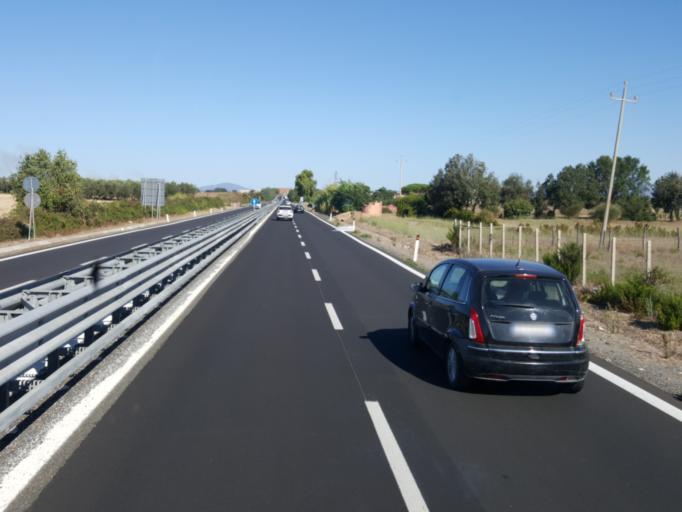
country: IT
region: Latium
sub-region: Provincia di Viterbo
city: Montalto di Castro
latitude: 42.3304
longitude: 11.6295
